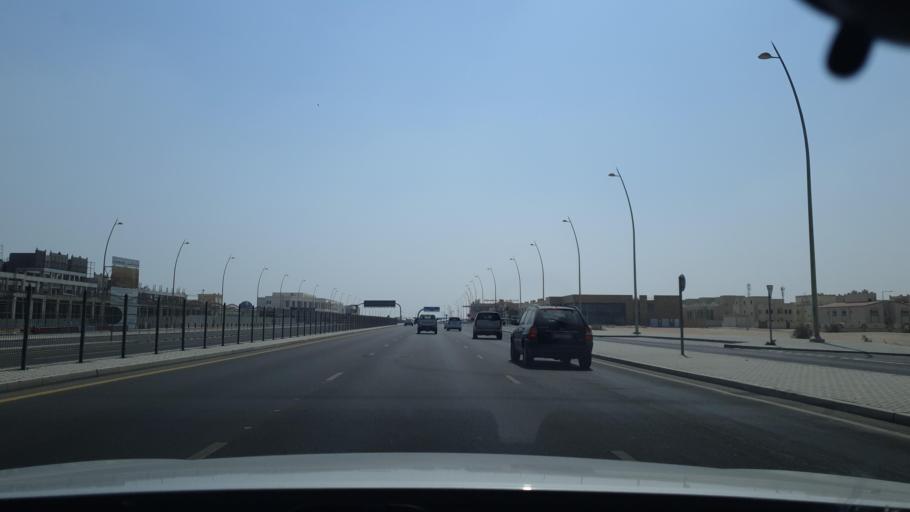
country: QA
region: Al Khawr
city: Al Khawr
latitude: 25.6714
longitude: 51.5009
